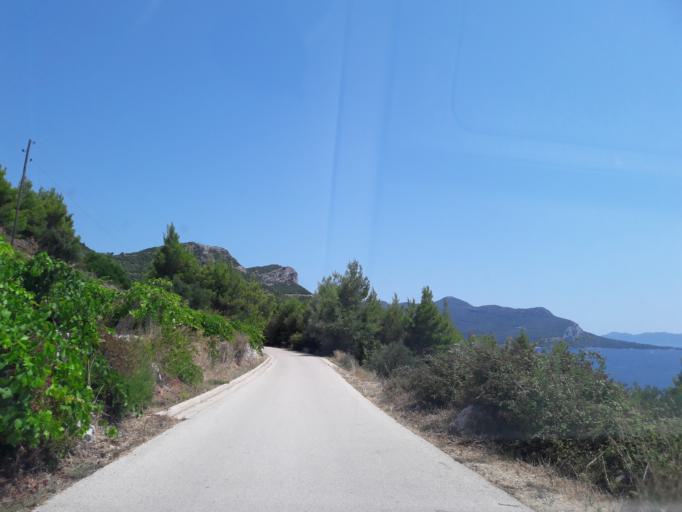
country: HR
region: Dubrovacko-Neretvanska
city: Blato
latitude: 42.9137
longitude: 17.4136
